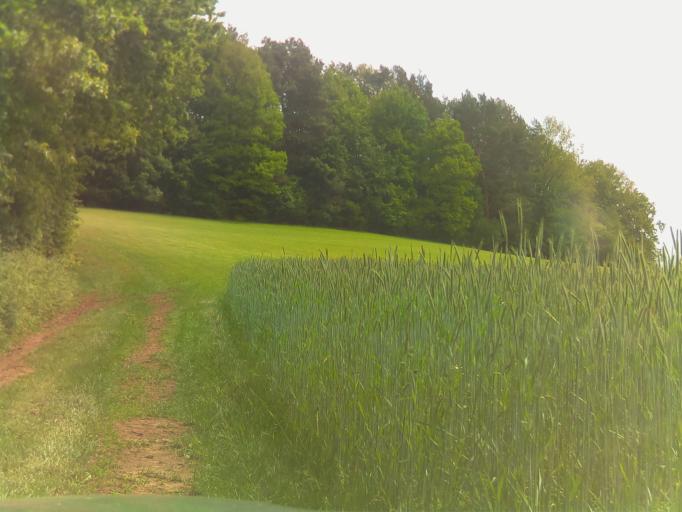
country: DE
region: Bavaria
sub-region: Regierungsbezirk Unterfranken
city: Aura im Sinngrund
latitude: 50.2163
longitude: 9.4976
